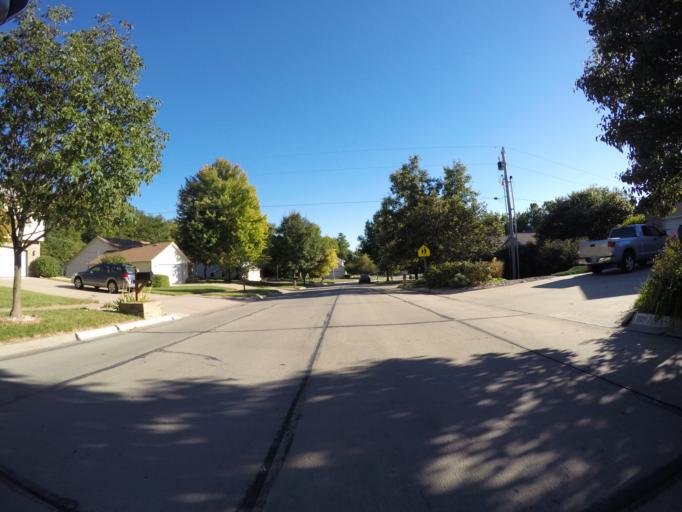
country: US
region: Kansas
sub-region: Riley County
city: Manhattan
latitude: 39.1977
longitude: -96.6276
